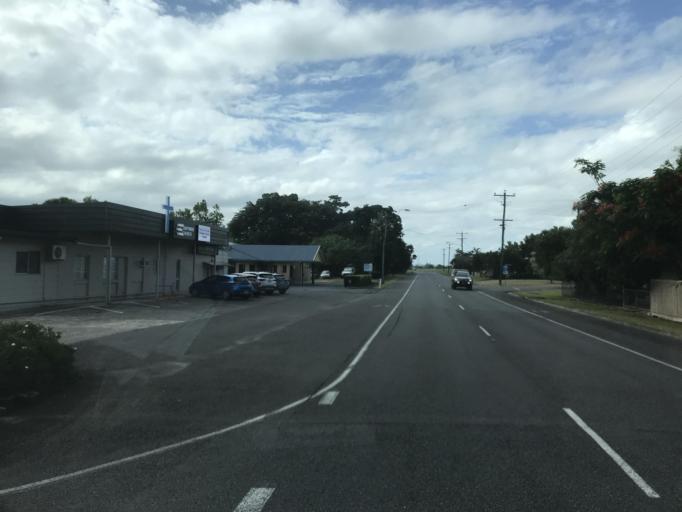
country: AU
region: Queensland
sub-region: Cassowary Coast
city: Innisfail
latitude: -17.5438
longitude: 146.0326
